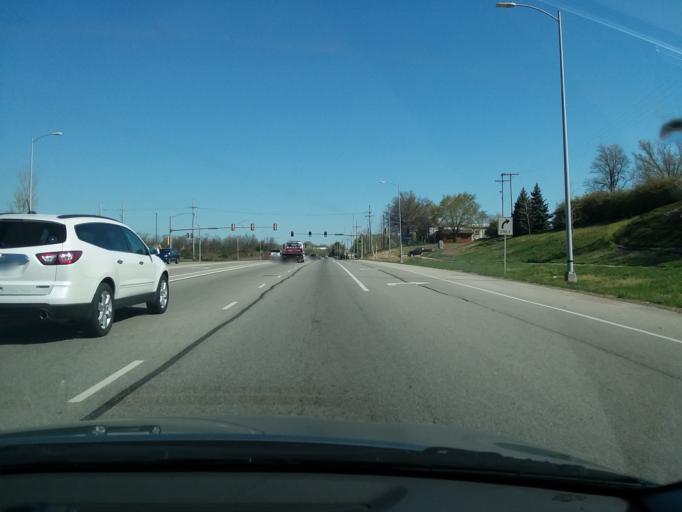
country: US
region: Kansas
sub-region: Johnson County
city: Olathe
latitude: 38.8862
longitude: -94.8345
